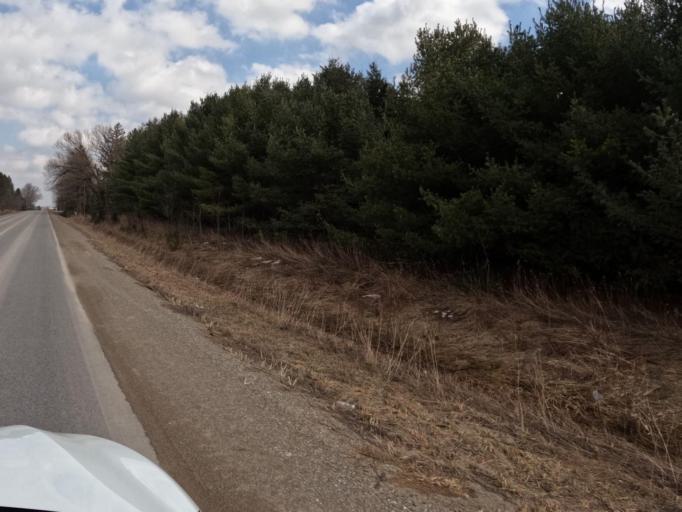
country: CA
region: Ontario
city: Shelburne
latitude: 44.0022
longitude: -80.2400
